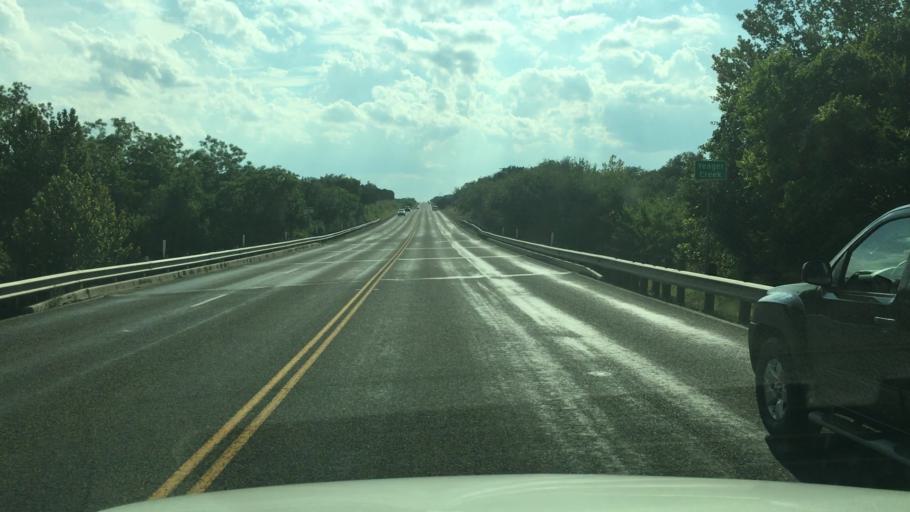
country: US
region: Texas
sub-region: Blanco County
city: Johnson City
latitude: 30.2106
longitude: -98.2849
